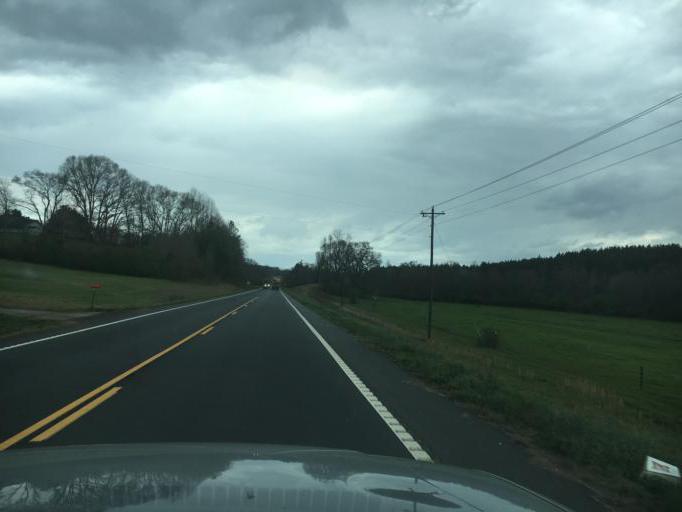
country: US
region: South Carolina
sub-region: Oconee County
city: Walhalla
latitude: 34.7871
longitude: -83.0203
